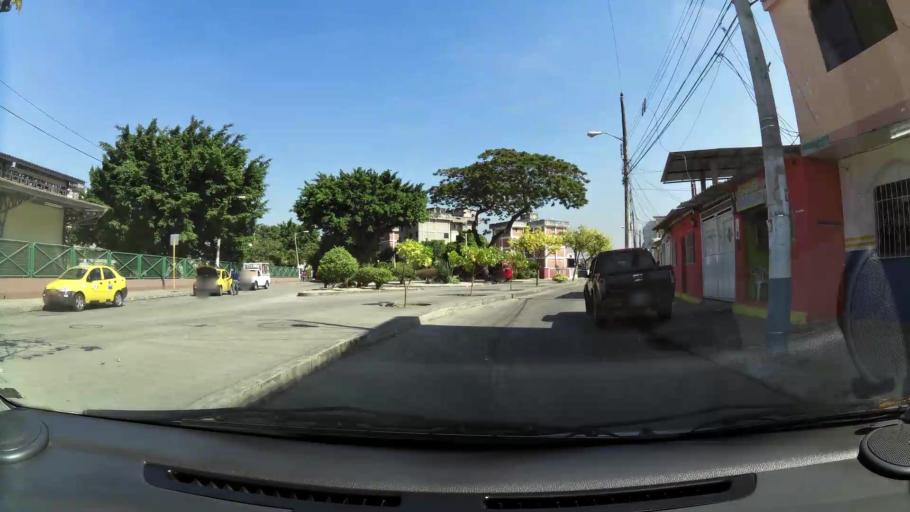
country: EC
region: Guayas
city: Eloy Alfaro
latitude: -2.1238
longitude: -79.8850
